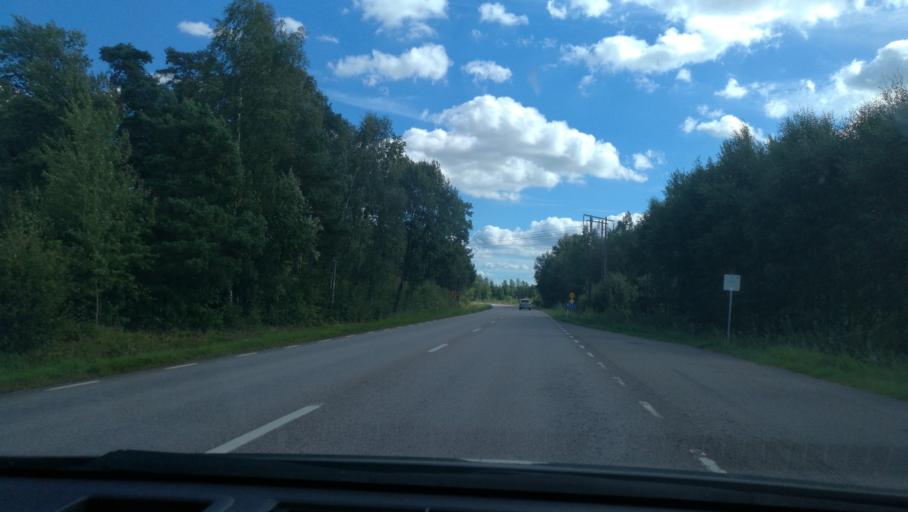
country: SE
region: Vaestra Goetaland
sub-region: Lidkopings Kommun
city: Vinninga
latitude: 58.4924
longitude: 13.2682
